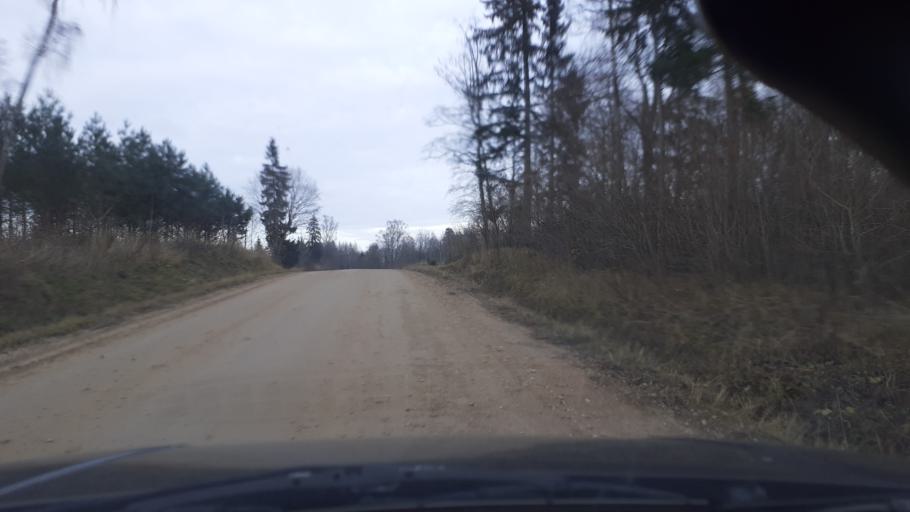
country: LV
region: Alsunga
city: Alsunga
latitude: 56.9637
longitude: 21.6538
